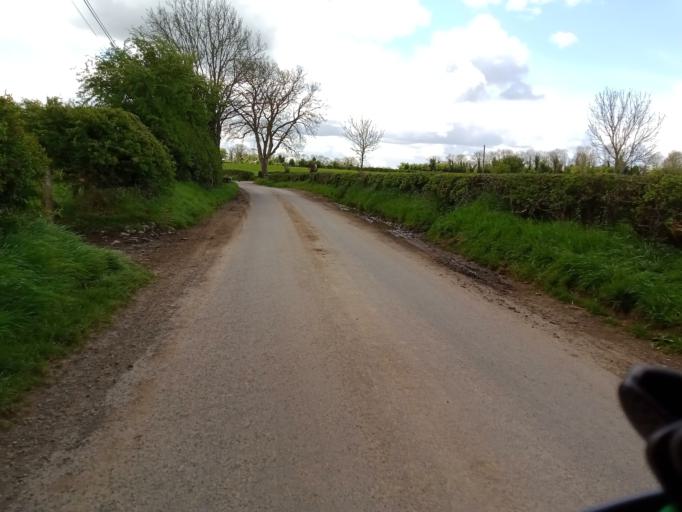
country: IE
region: Leinster
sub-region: Kilkenny
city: Thomastown
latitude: 52.5944
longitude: -7.1507
